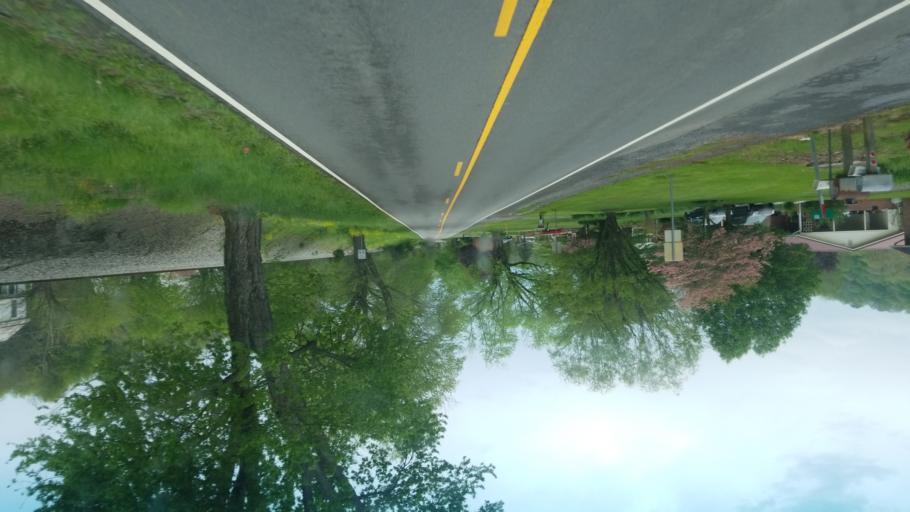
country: US
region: Virginia
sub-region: Smyth County
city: Chilhowie
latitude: 36.8106
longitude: -81.6309
